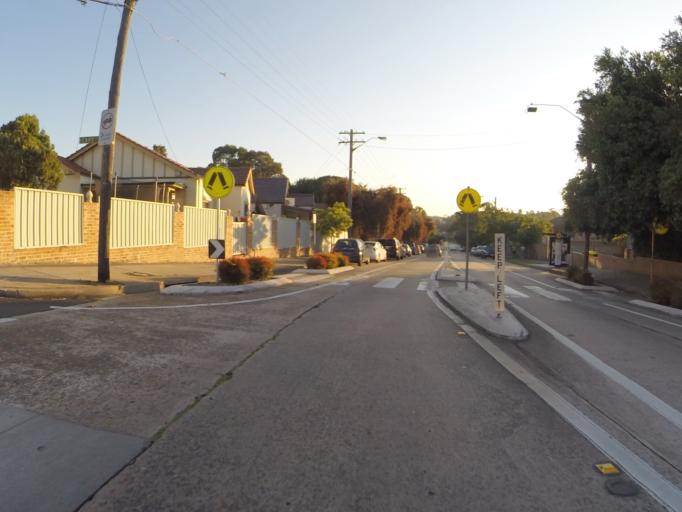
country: AU
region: New South Wales
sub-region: Marrickville
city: Marrickville
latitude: -33.9169
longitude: 151.1493
